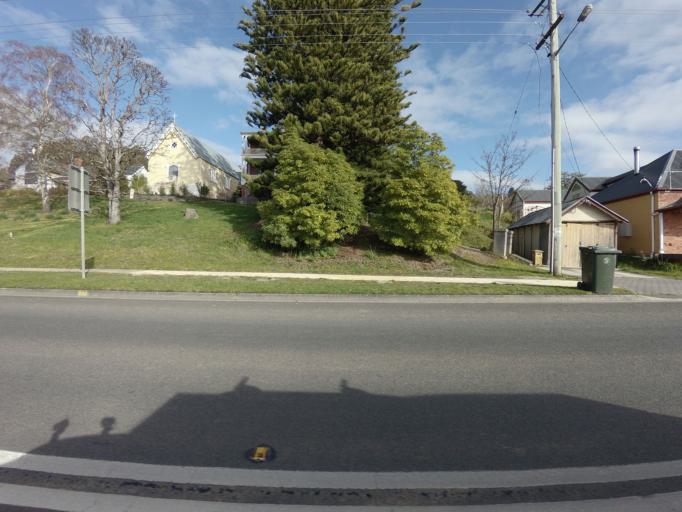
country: AU
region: Tasmania
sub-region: Huon Valley
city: Franklin
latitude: -43.0946
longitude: 147.0075
